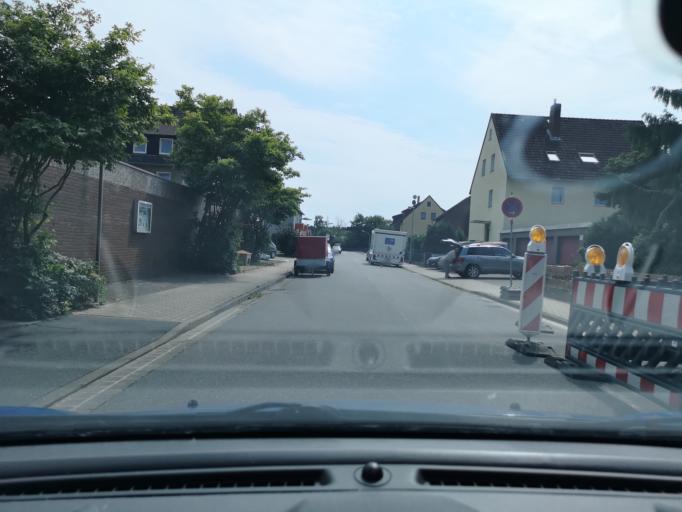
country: DE
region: Lower Saxony
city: Langenhagen
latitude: 52.4348
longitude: 9.6748
